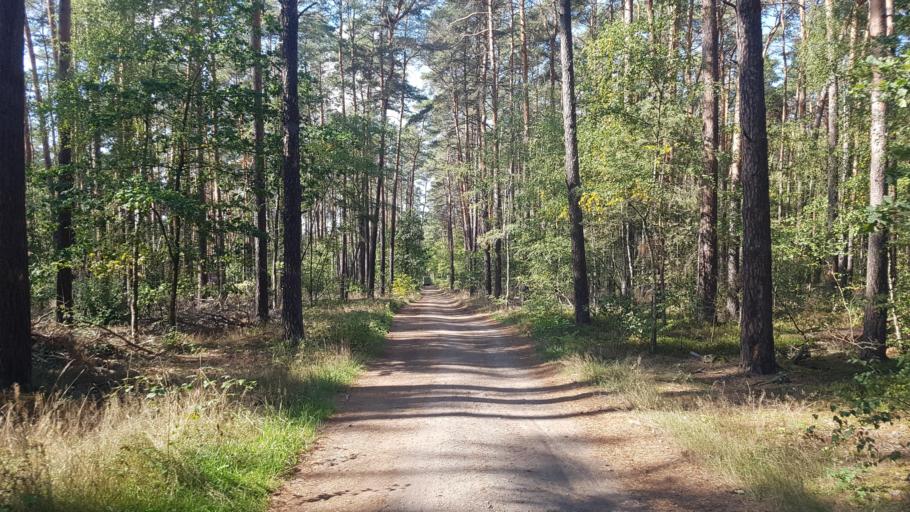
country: DE
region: Brandenburg
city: Lebusa
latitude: 51.8216
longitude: 13.4215
